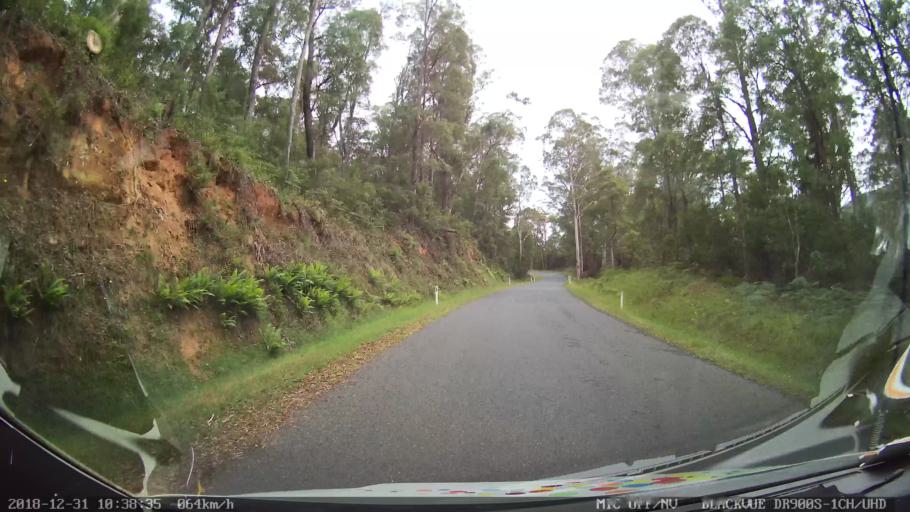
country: AU
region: New South Wales
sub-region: Snowy River
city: Jindabyne
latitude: -36.4060
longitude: 148.1774
